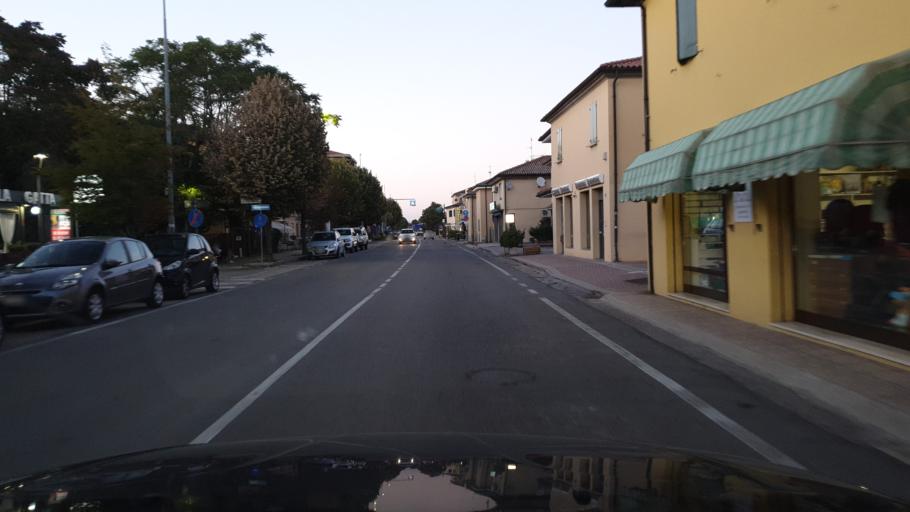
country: IT
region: Emilia-Romagna
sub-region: Provincia di Bologna
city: Altedo
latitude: 44.6665
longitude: 11.4879
